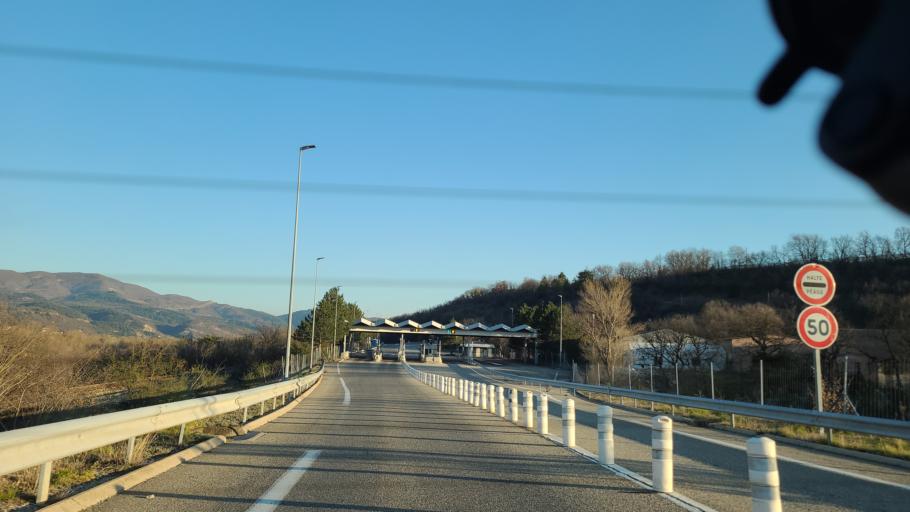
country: FR
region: Provence-Alpes-Cote d'Azur
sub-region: Departement des Alpes-de-Haute-Provence
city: Peipin
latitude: 44.1256
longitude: 5.9835
